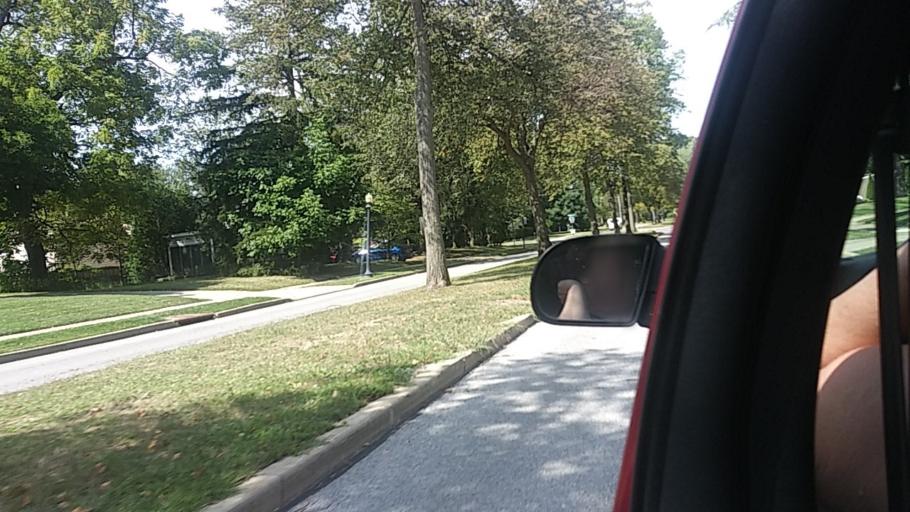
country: US
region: Ohio
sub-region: Summit County
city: Fairlawn
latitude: 41.1158
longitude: -81.5613
